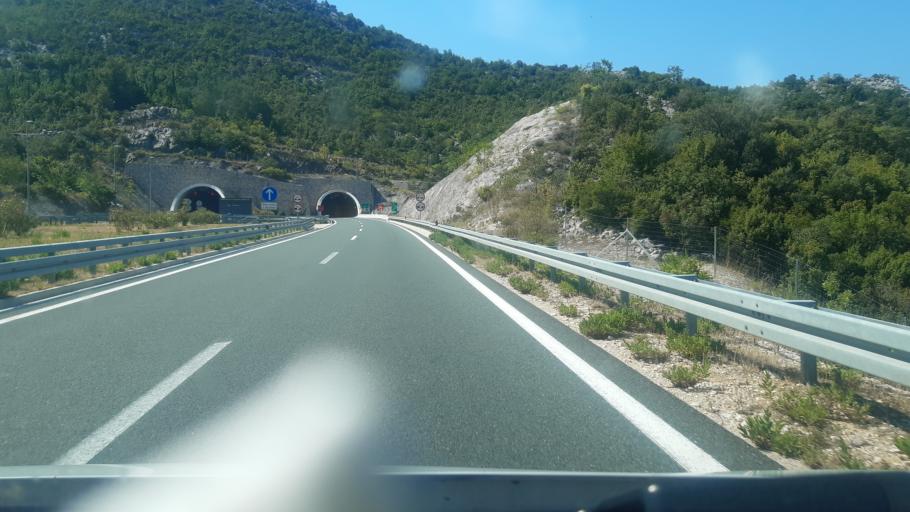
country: BA
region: Federation of Bosnia and Herzegovina
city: Ljubuski
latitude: 43.1297
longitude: 17.4842
